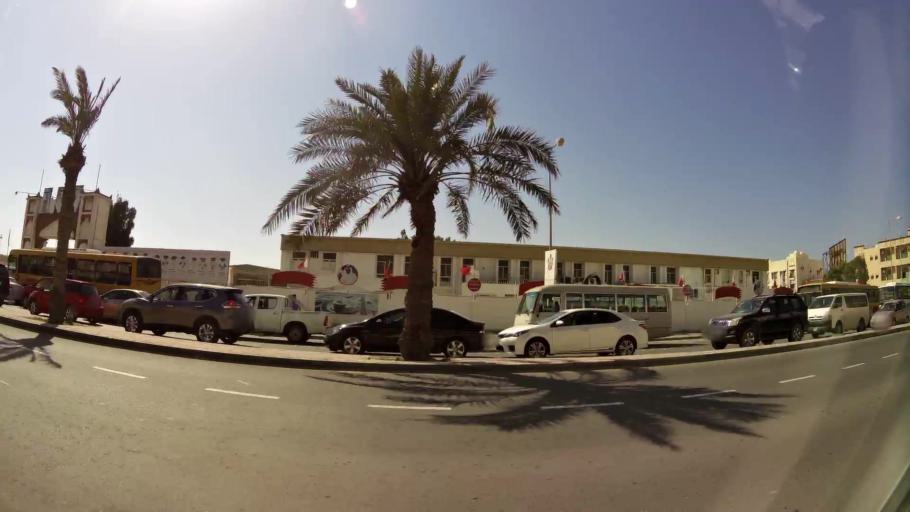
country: BH
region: Manama
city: Manama
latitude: 26.2089
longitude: 50.5756
